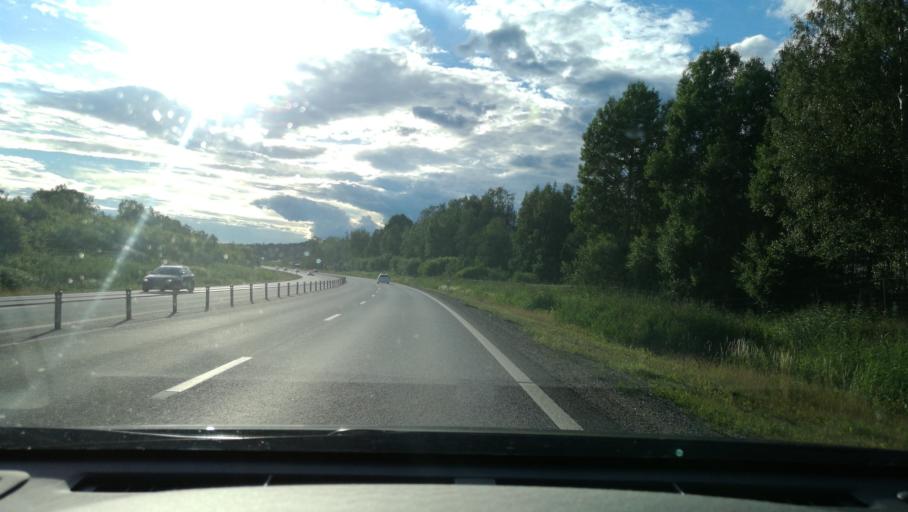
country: SE
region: OEstergoetland
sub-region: Norrkopings Kommun
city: Svartinge
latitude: 58.6434
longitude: 16.0831
